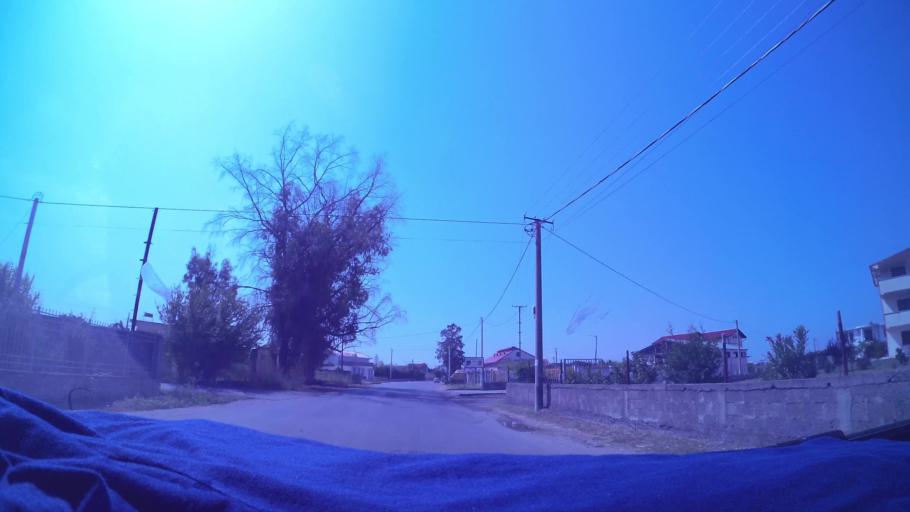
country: AL
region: Durres
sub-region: Rrethi i Durresit
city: Xhafzotaj
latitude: 41.3599
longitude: 19.5491
